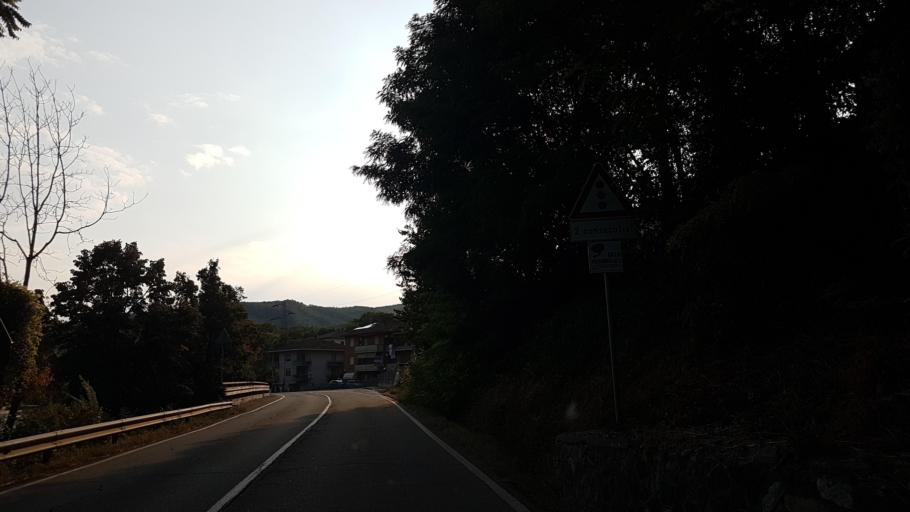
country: IT
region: Emilia-Romagna
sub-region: Provincia di Parma
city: Solignano
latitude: 44.6158
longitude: 9.9802
